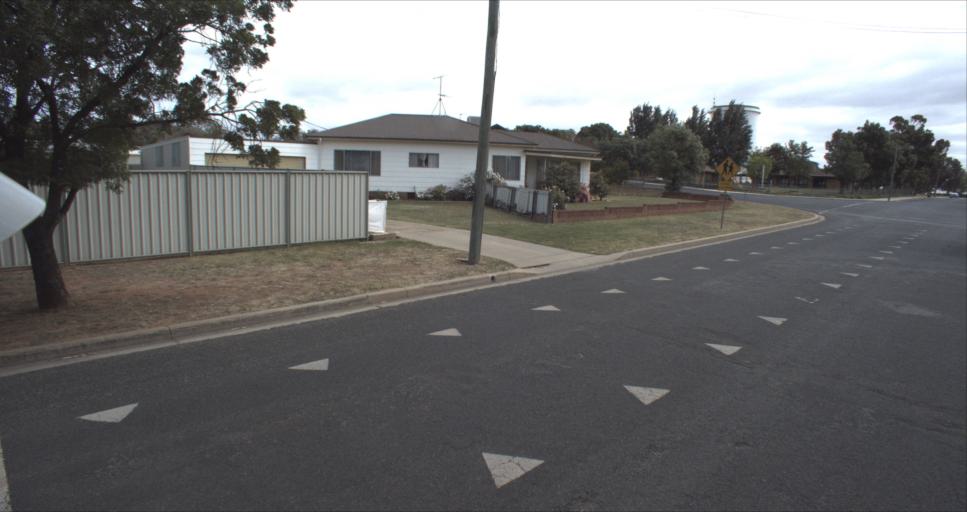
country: AU
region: New South Wales
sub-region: Leeton
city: Leeton
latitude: -34.5634
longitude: 146.3973
